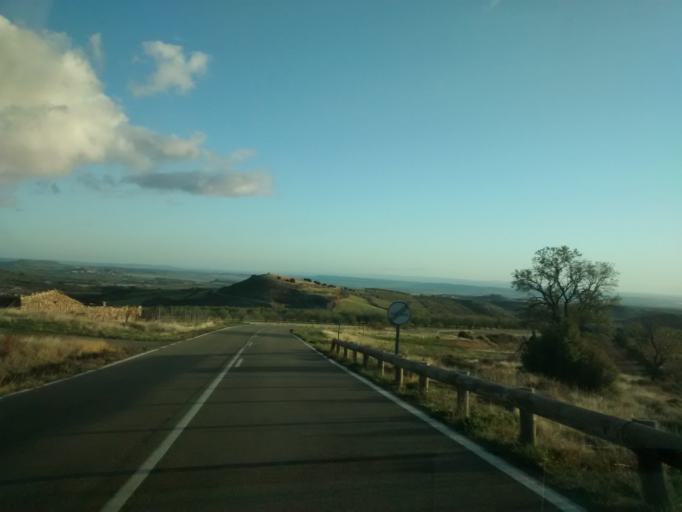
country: ES
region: Aragon
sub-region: Provincia de Huesca
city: Loarre
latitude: 42.3174
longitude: -0.6168
